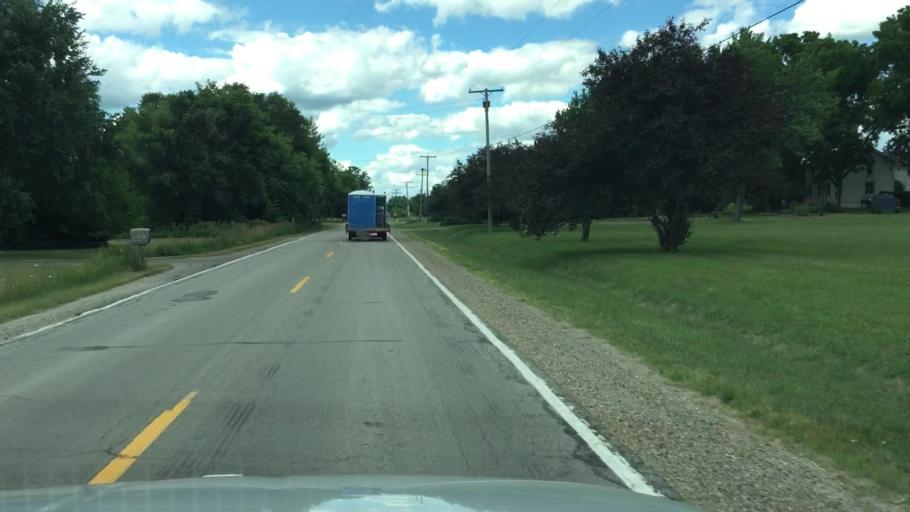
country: US
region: Michigan
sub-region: Macomb County
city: Armada
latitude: 42.9073
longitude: -82.9453
